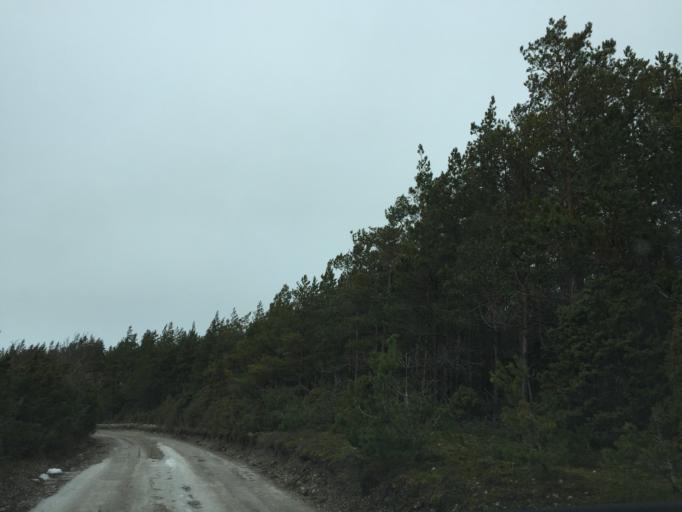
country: EE
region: Saare
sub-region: Kuressaare linn
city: Kuressaare
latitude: 58.5010
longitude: 21.9191
